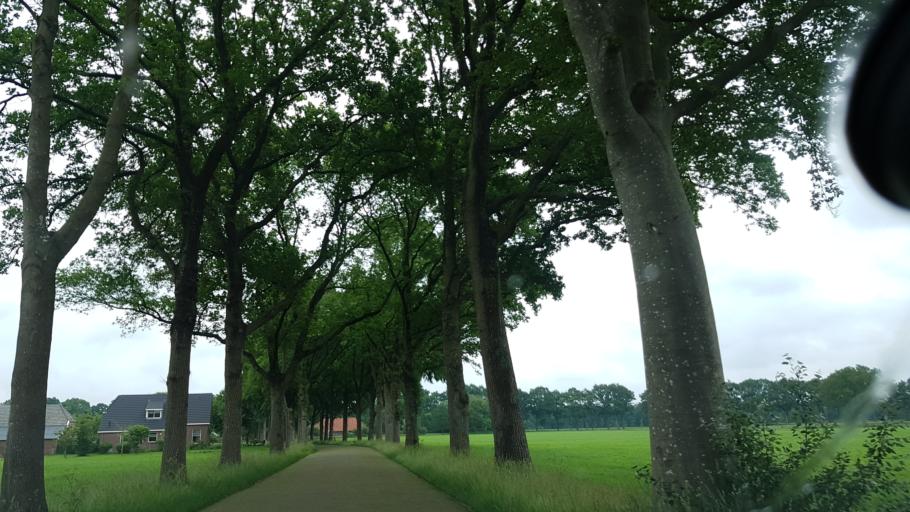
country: NL
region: Drenthe
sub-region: Gemeente Tynaarlo
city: Tynaarlo
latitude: 53.0495
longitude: 6.6332
